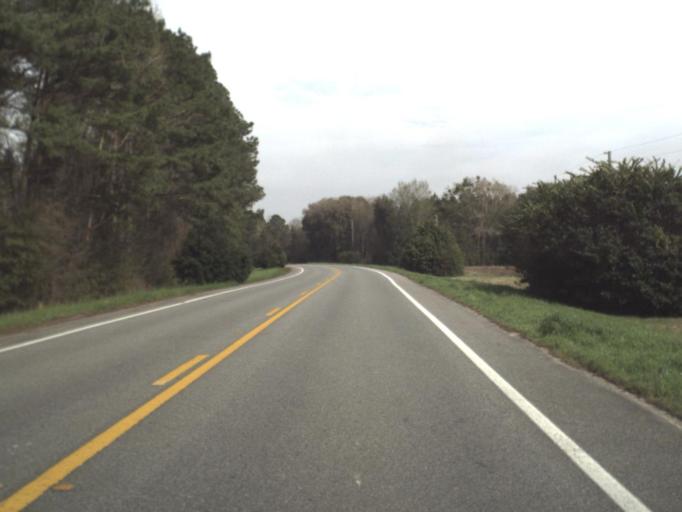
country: US
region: Florida
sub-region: Jefferson County
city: Monticello
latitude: 30.5303
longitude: -83.8207
